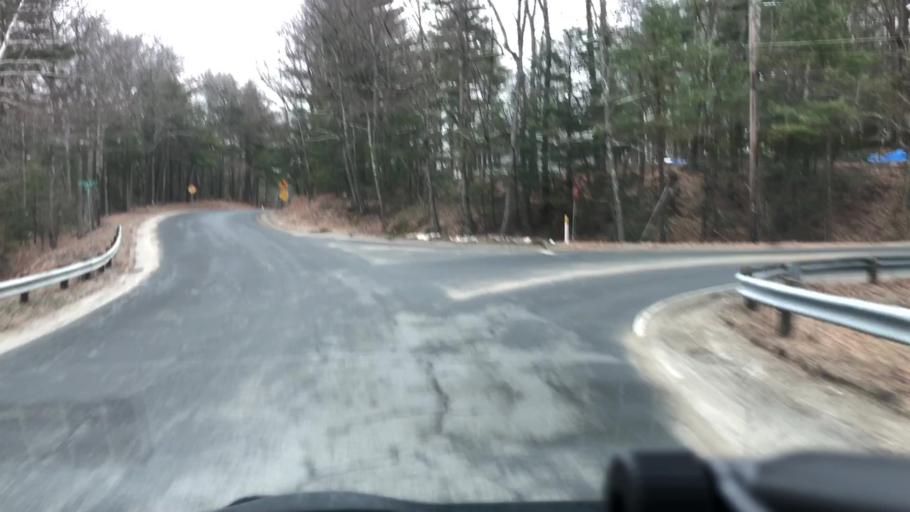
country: US
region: Massachusetts
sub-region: Hampshire County
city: Southampton
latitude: 42.2587
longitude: -72.7322
